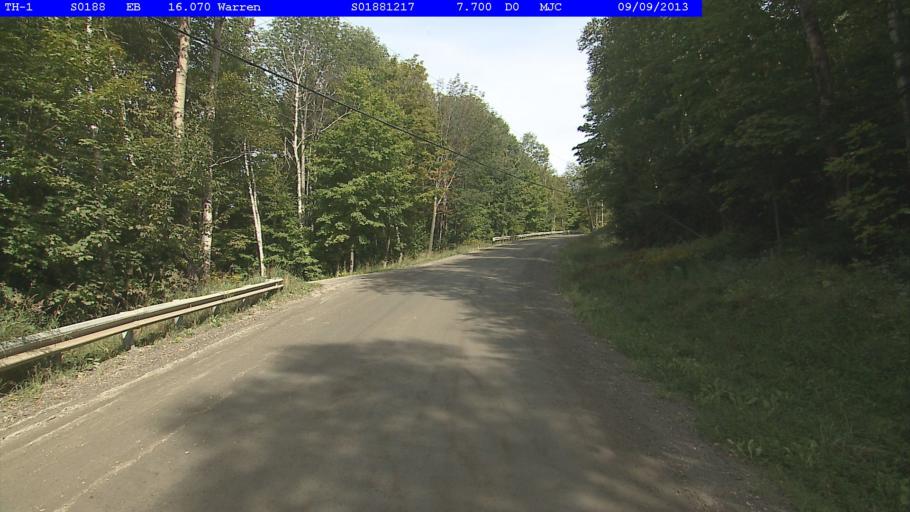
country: US
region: Vermont
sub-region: Washington County
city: Northfield
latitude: 44.1089
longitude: -72.8017
